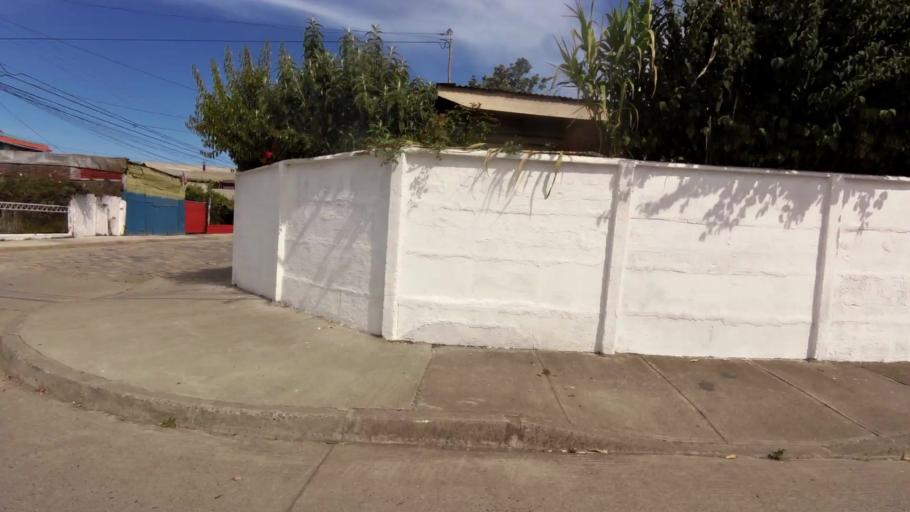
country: CL
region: Biobio
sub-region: Provincia de Concepcion
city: Talcahuano
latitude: -36.7229
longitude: -73.1163
